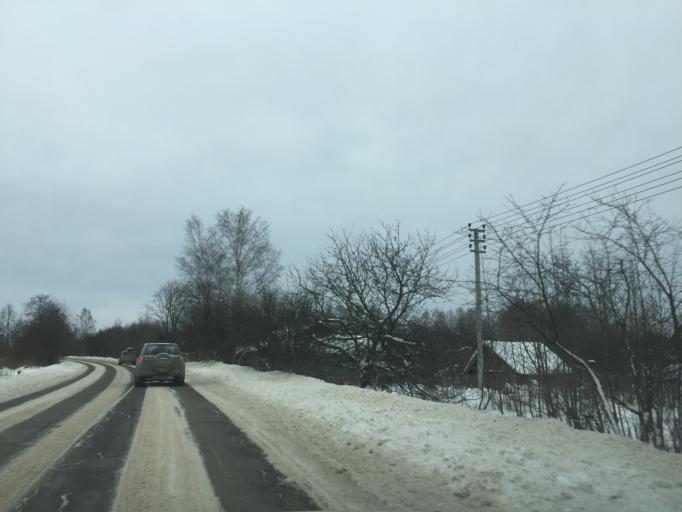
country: RU
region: Leningrad
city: Imeni Sverdlova
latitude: 59.7885
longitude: 30.7080
